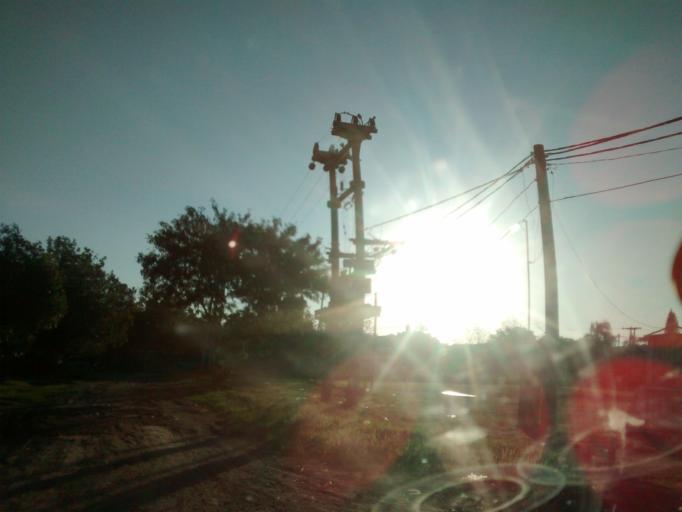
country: AR
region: Chaco
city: Fontana
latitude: -27.4394
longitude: -59.0199
